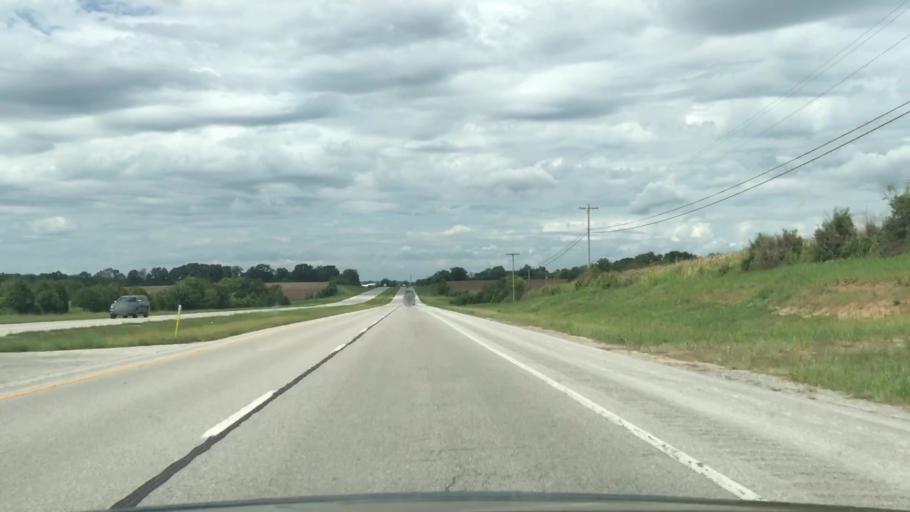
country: US
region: Kentucky
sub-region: Todd County
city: Elkton
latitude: 36.8244
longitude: -87.2076
